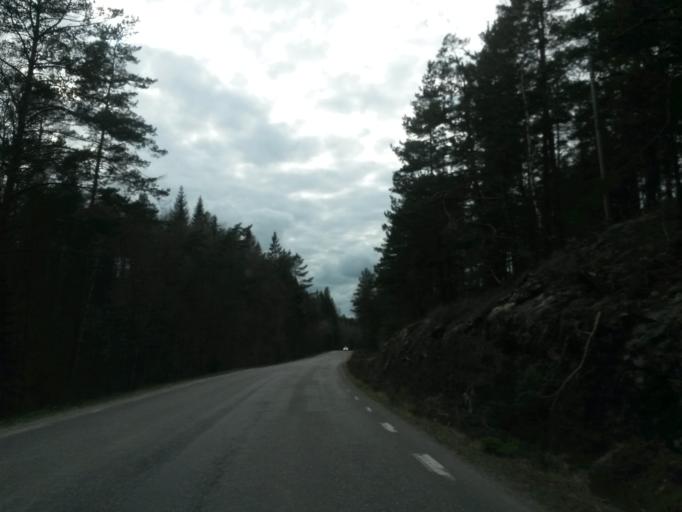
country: SE
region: Vaestra Goetaland
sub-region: Vargarda Kommun
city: Jonstorp
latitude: 57.9481
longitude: 12.6364
